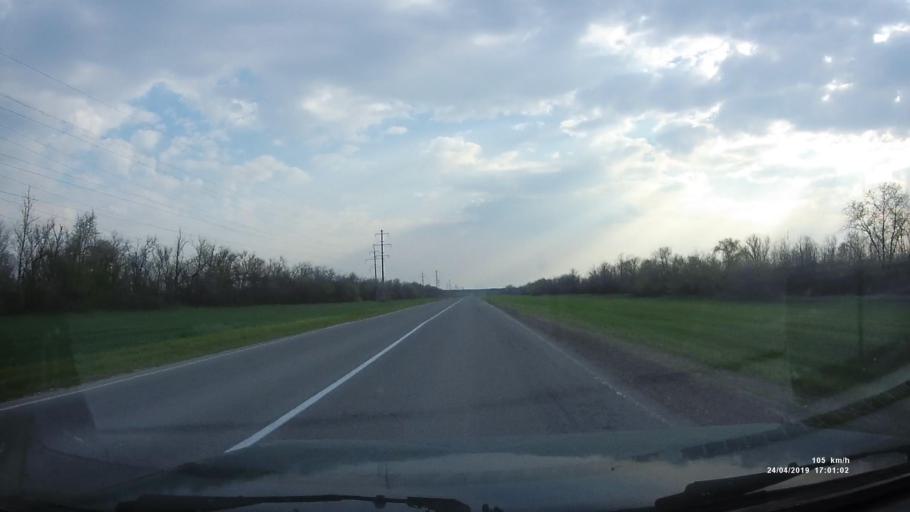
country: RU
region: Rostov
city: Proletarsk
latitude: 46.5976
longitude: 41.6307
